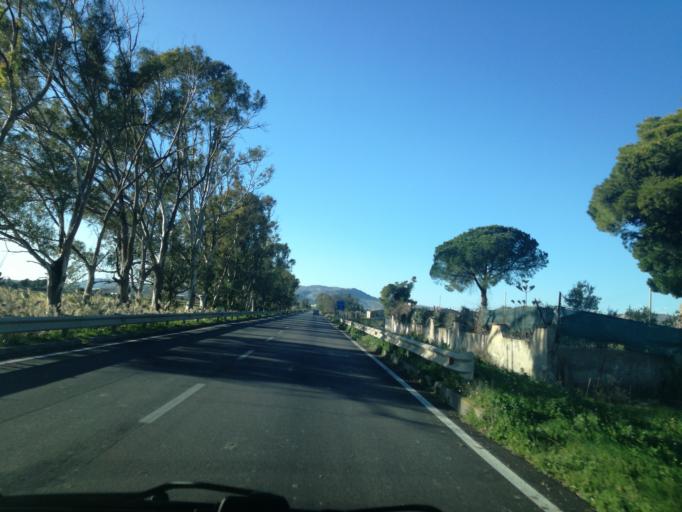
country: IT
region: Sicily
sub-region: Provincia di Caltanissetta
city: Butera
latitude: 37.1157
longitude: 14.1437
